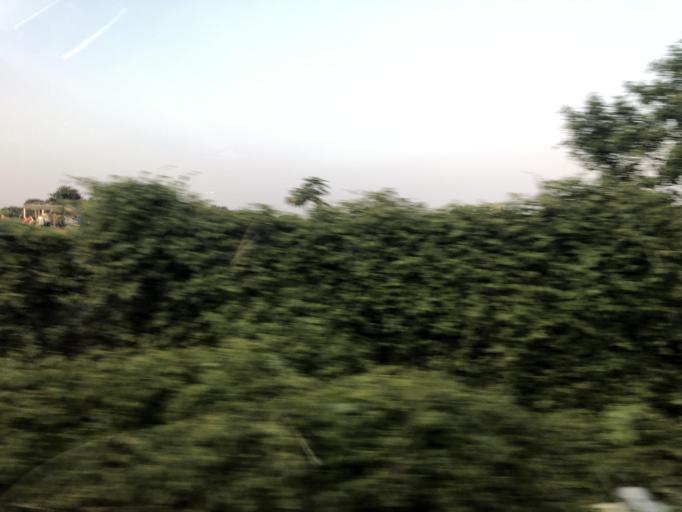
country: TW
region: Taiwan
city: Xinying
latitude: 23.1591
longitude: 120.2718
